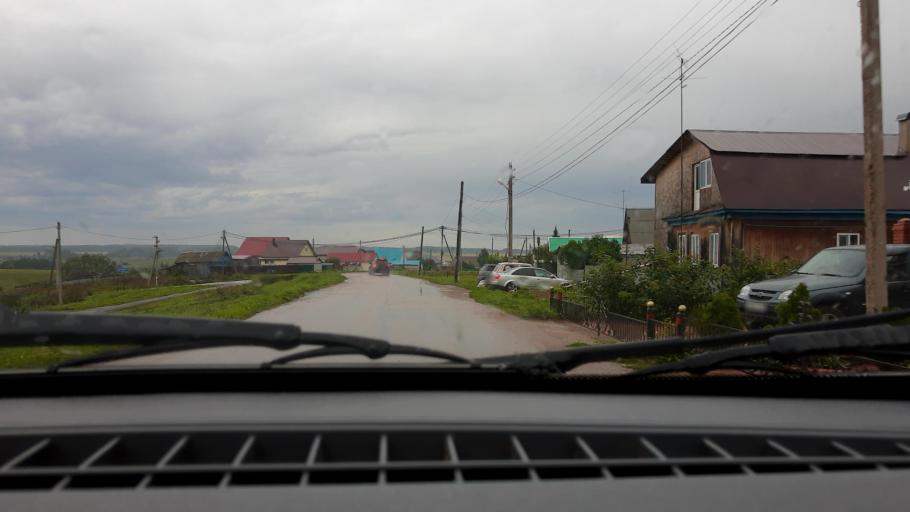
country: RU
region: Bashkortostan
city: Avdon
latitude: 54.8164
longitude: 55.6942
